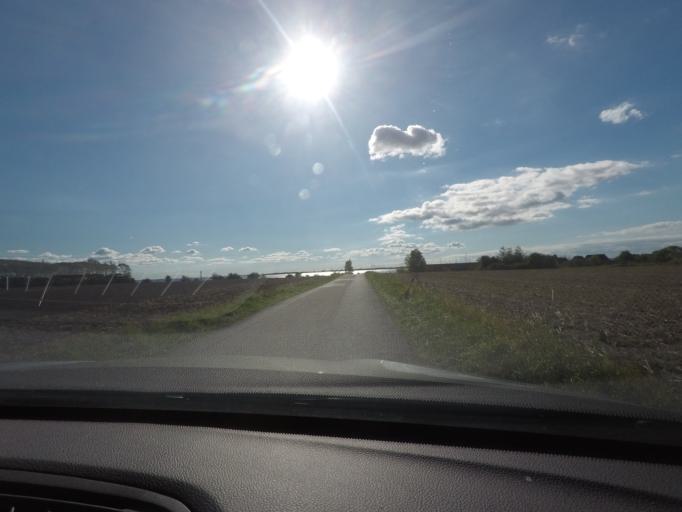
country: DK
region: Zealand
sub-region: Lolland Kommune
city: Maribo
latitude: 54.9732
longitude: 11.5187
